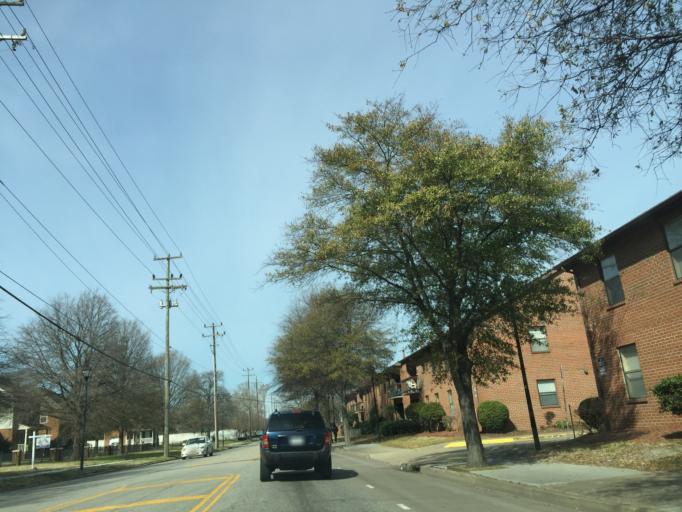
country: US
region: Virginia
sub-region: City of Norfolk
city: Norfolk
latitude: 36.8584
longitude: -76.2791
